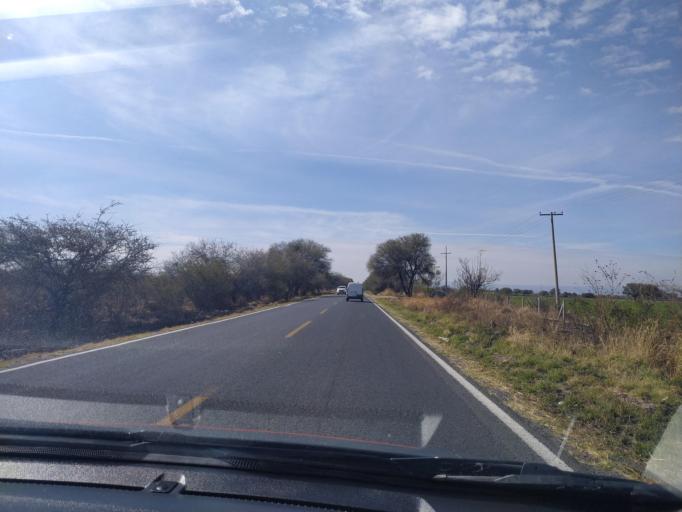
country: MX
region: Guanajuato
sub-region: San Francisco del Rincon
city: San Ignacio de Hidalgo
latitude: 20.9239
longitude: -101.8539
